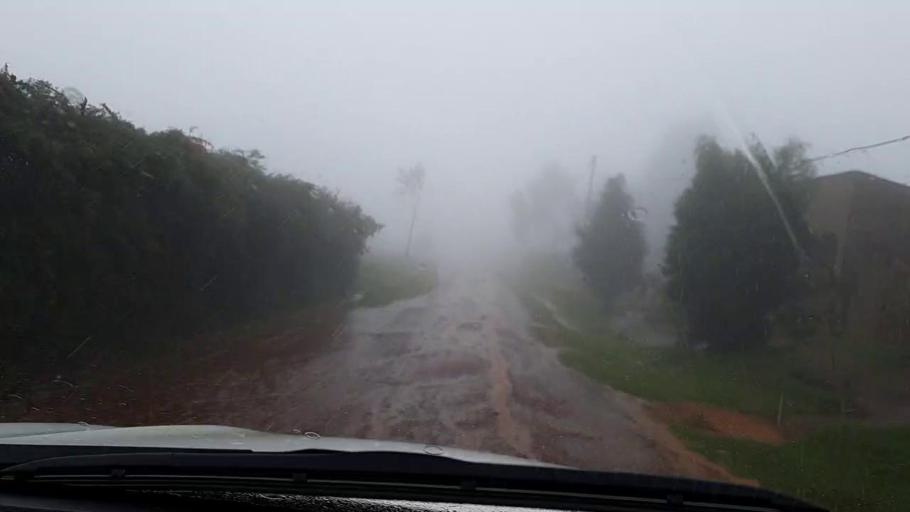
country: RW
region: Northern Province
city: Byumba
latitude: -1.7322
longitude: 30.0213
